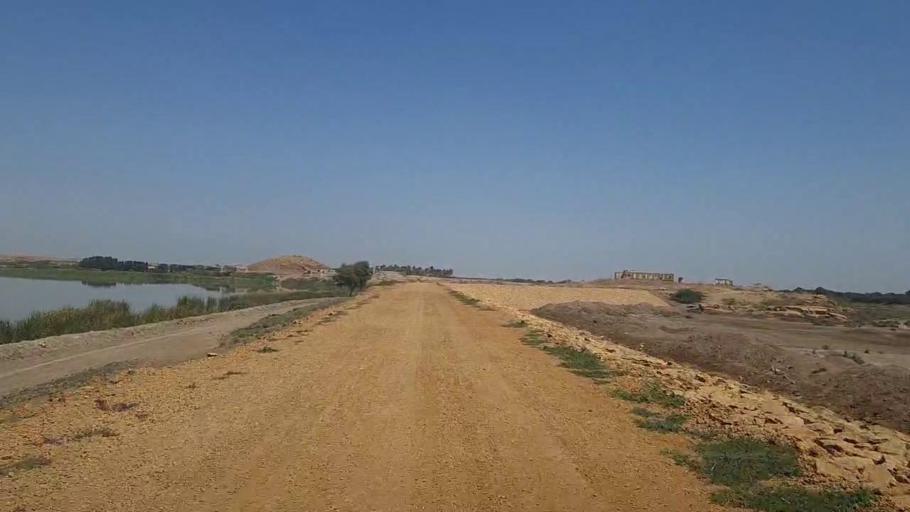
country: PK
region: Sindh
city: Thatta
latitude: 24.8059
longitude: 68.0029
